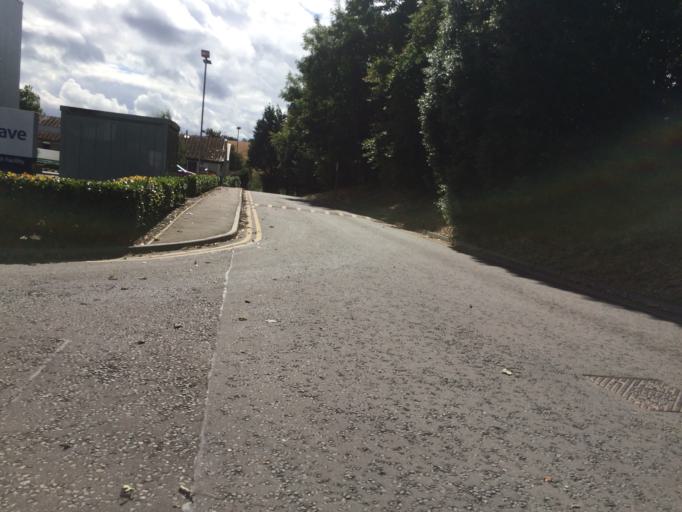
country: GB
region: Scotland
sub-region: Edinburgh
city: Edinburgh
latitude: 55.9223
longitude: -3.1792
